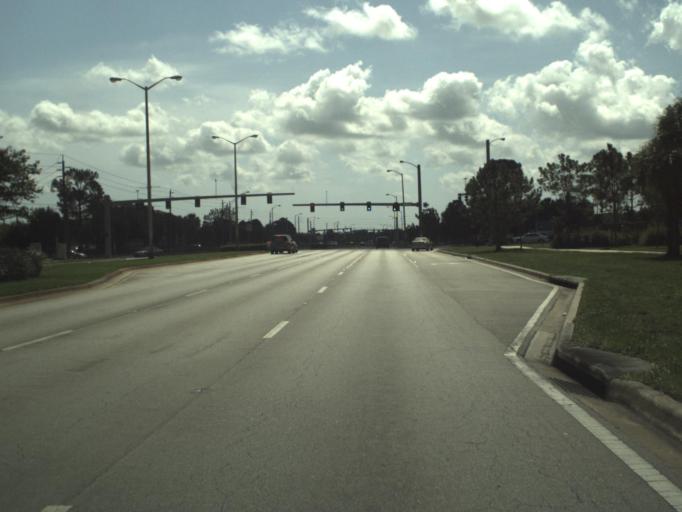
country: US
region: Florida
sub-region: Saint Lucie County
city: Port Saint Lucie
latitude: 27.2645
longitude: -80.4039
